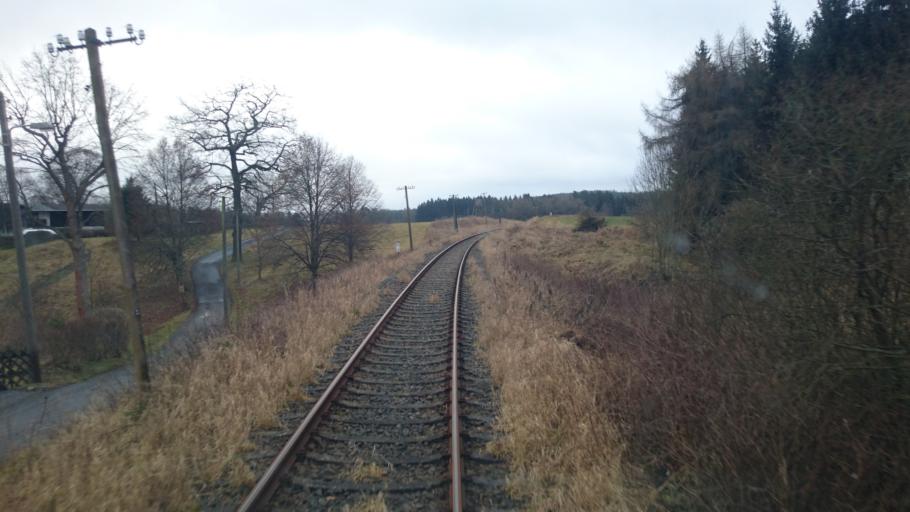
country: DE
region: Saxony
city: Muhltroff
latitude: 50.5601
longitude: 11.8998
